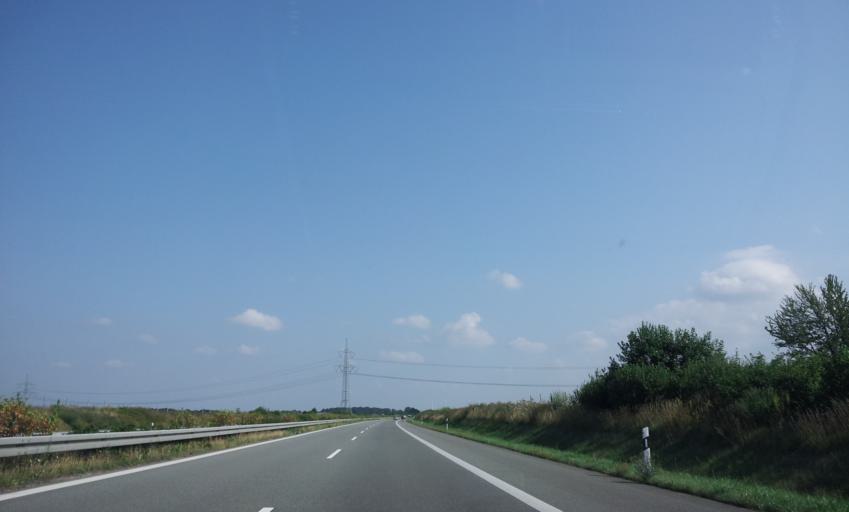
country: DE
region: Mecklenburg-Vorpommern
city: Dersekow
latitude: 54.0435
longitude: 13.2631
